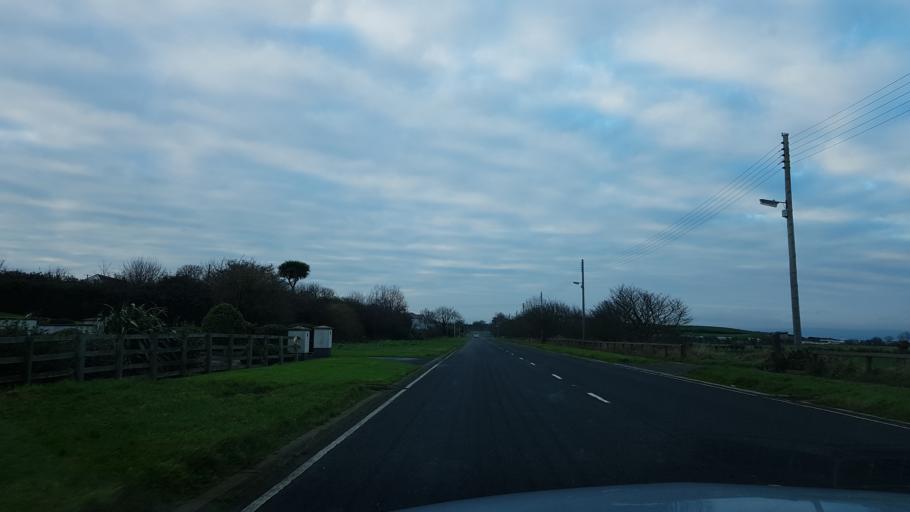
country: GB
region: Northern Ireland
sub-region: Down District
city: Donaghadee
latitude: 54.6717
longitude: -5.5932
